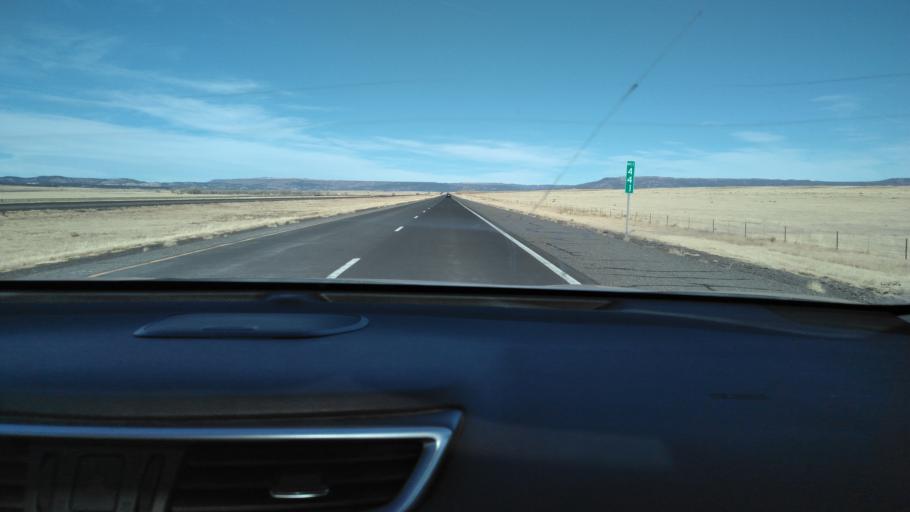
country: US
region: New Mexico
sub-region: Colfax County
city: Raton
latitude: 36.7351
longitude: -104.4566
